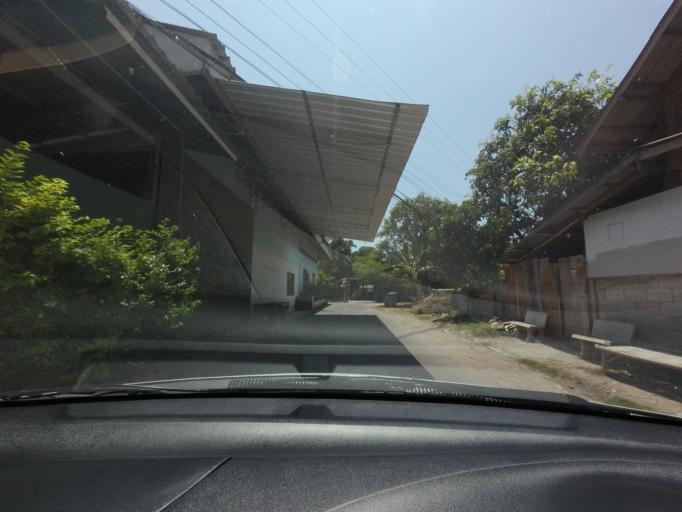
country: TH
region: Samut Songkhram
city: Bang Khon Thi
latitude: 13.4706
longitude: 99.9712
